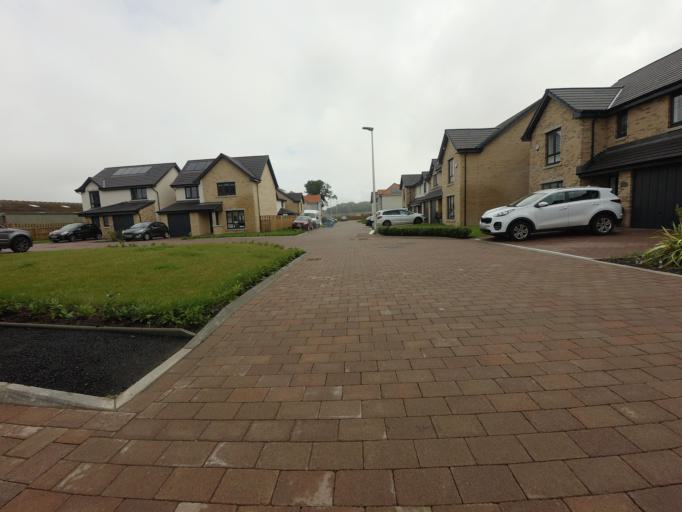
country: GB
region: Scotland
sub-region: West Lothian
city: Kirknewton
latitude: 55.9031
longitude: -3.4396
